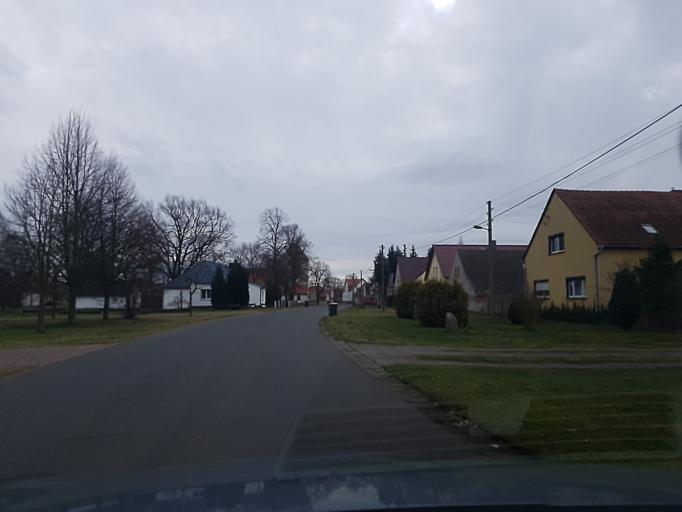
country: DE
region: Brandenburg
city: Schilda
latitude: 51.6215
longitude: 13.3545
